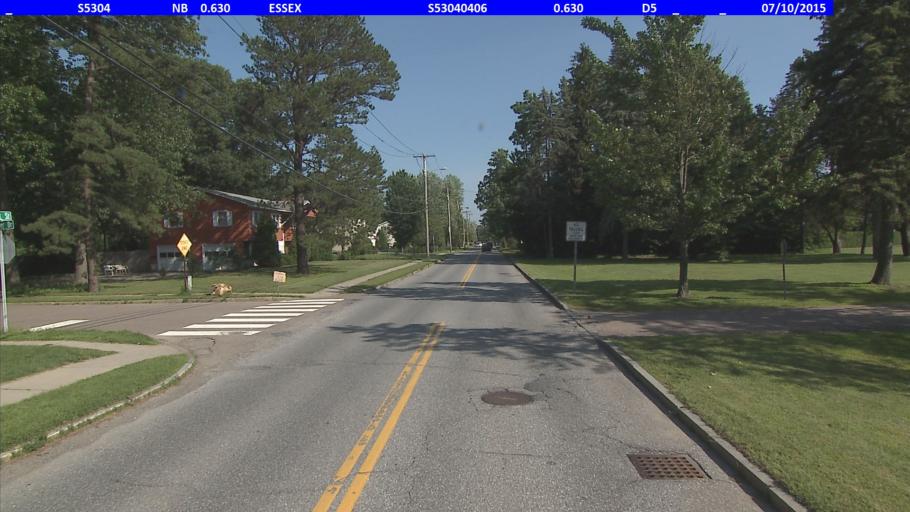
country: US
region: Vermont
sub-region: Chittenden County
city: Essex Junction
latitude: 44.4914
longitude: -73.1254
